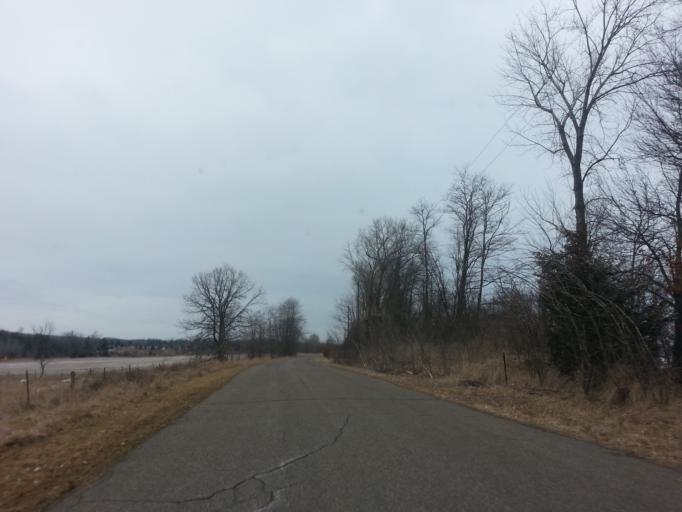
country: US
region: Wisconsin
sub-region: Saint Croix County
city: Hudson
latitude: 44.9811
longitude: -92.7741
